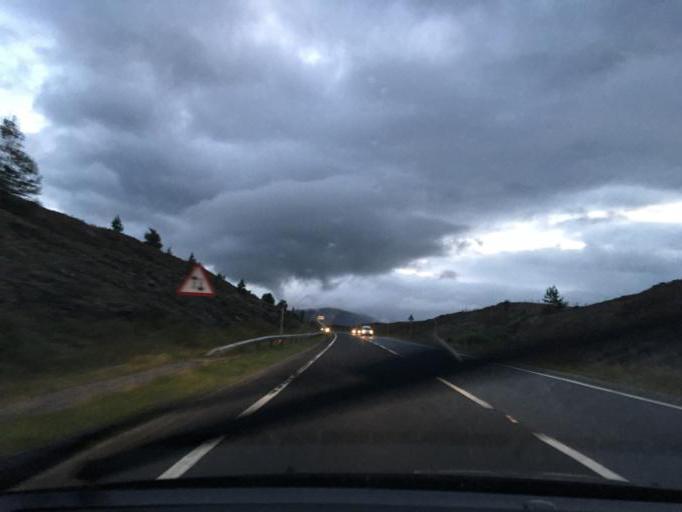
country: GB
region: Scotland
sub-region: Highland
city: Kingussie
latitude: 56.9610
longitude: -4.2055
